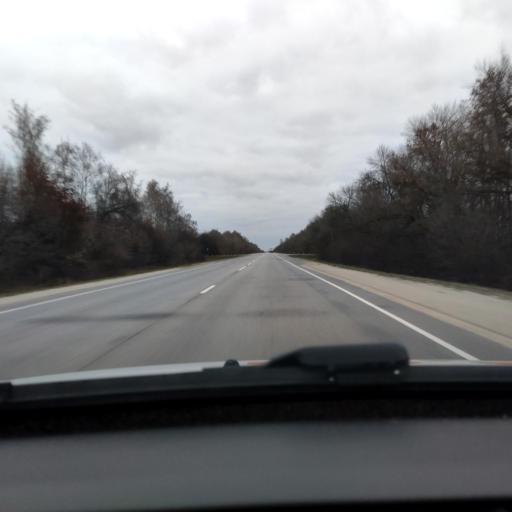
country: RU
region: Lipetsk
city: Borinskoye
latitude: 52.3708
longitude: 39.2091
